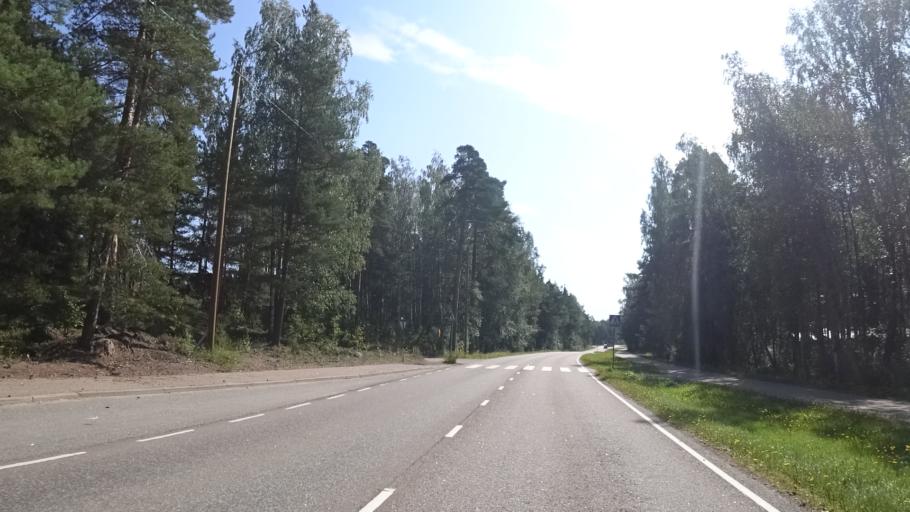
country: FI
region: Kymenlaakso
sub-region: Kotka-Hamina
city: Karhula
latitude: 60.5010
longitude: 26.9654
